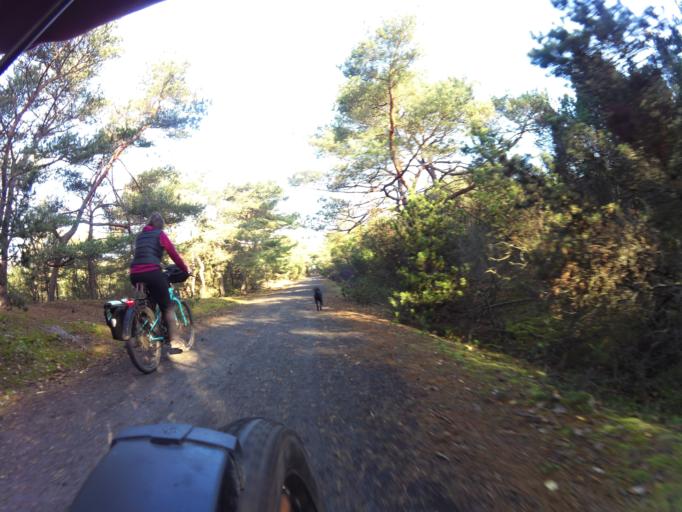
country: PL
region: Pomeranian Voivodeship
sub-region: Powiat pucki
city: Hel
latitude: 54.6034
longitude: 18.8175
